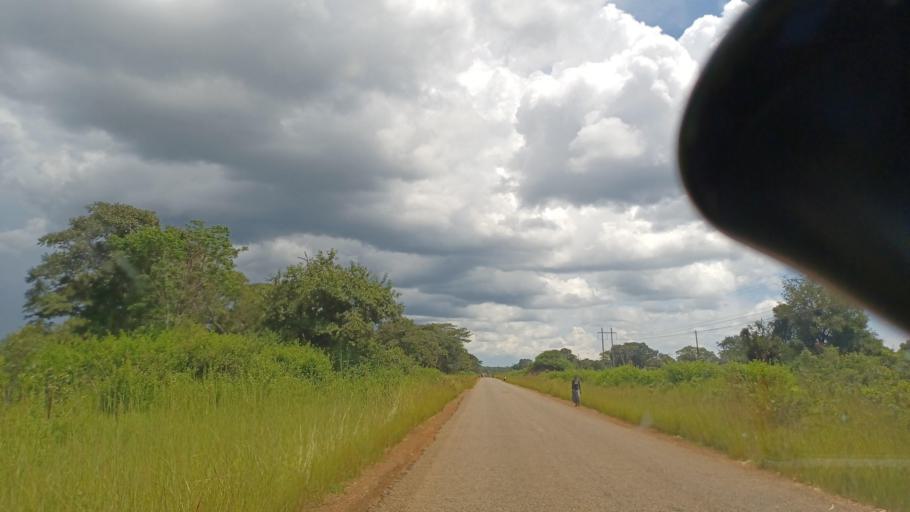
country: ZM
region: North-Western
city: Solwezi
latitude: -12.7651
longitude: 26.0187
